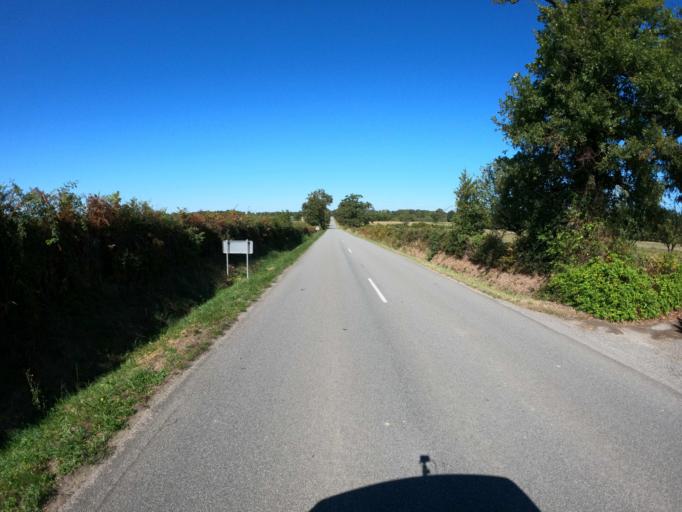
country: FR
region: Limousin
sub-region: Departement de la Haute-Vienne
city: Le Dorat
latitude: 46.2704
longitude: 1.0247
